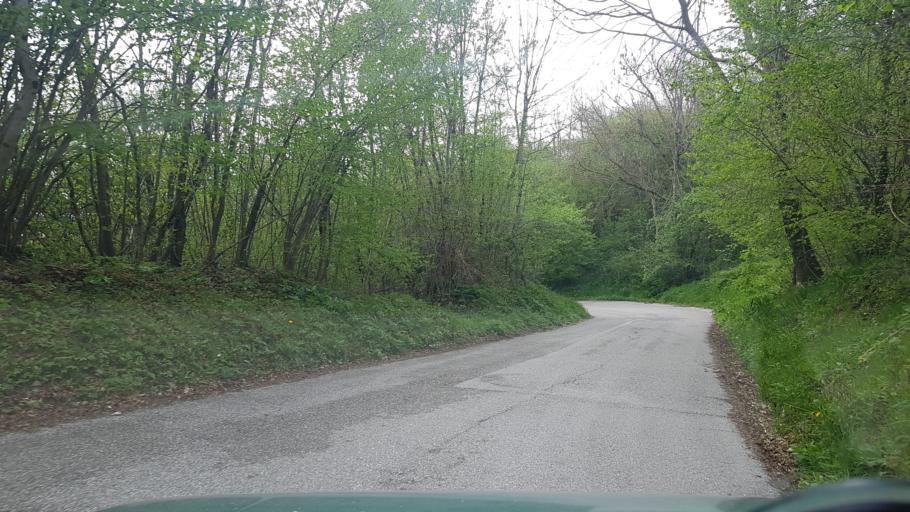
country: IT
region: Friuli Venezia Giulia
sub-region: Provincia di Udine
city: Attimis
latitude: 46.2050
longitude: 13.3531
